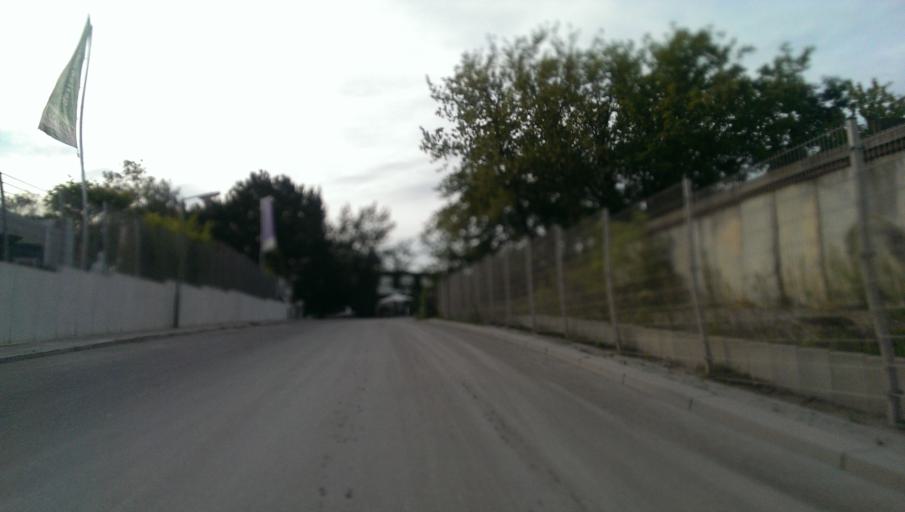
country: DE
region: Berlin
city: Lichterfelde
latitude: 52.4131
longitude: 13.2877
